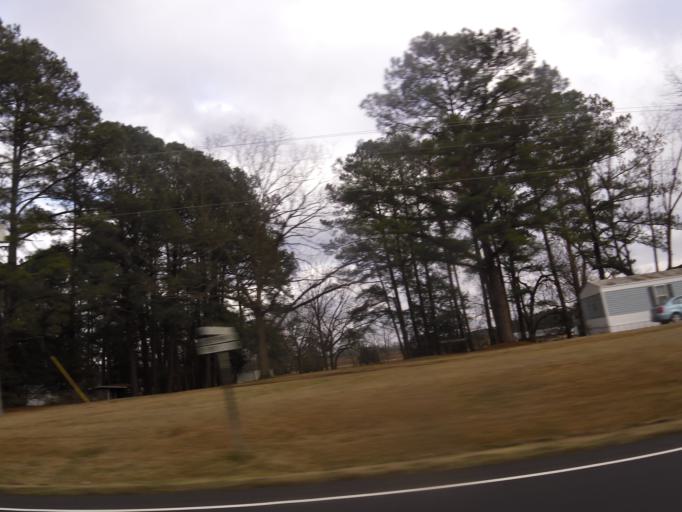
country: US
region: North Carolina
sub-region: Nash County
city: Rocky Mount
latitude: 35.8887
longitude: -77.7411
